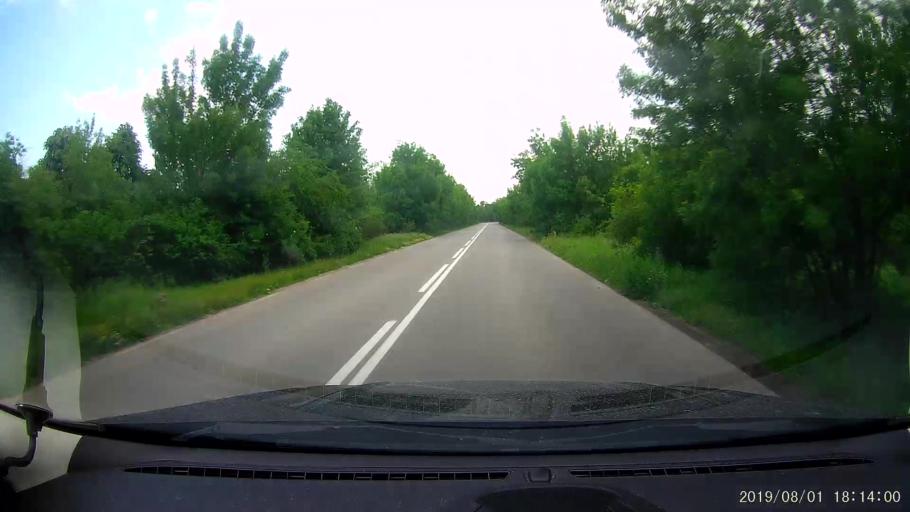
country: BG
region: Silistra
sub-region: Obshtina Dulovo
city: Dulovo
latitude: 43.7779
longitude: 27.1299
